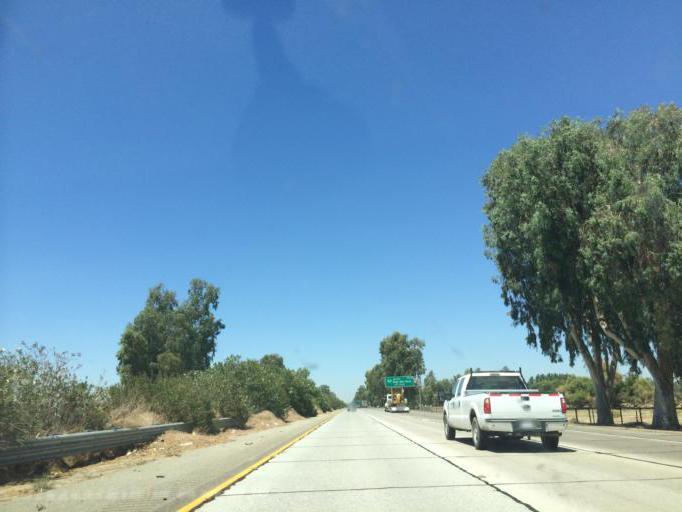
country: US
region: California
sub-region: Kern County
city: Greenfield
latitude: 35.1897
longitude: -119.0073
